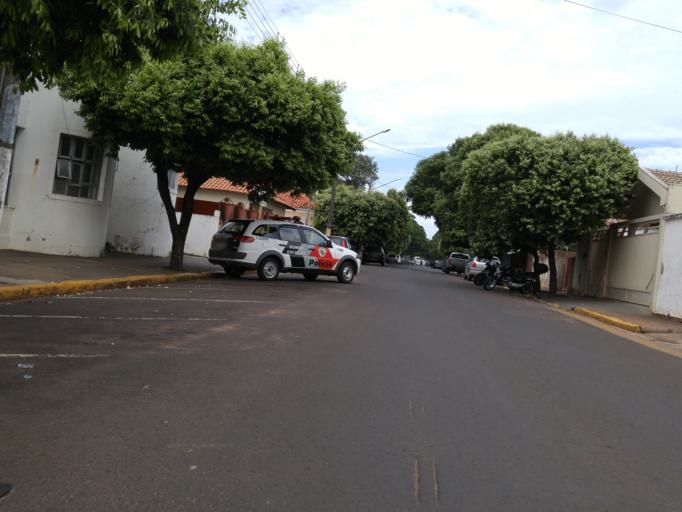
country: BR
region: Sao Paulo
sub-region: Paraguacu Paulista
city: Paraguacu Paulista
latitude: -22.4160
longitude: -50.5785
